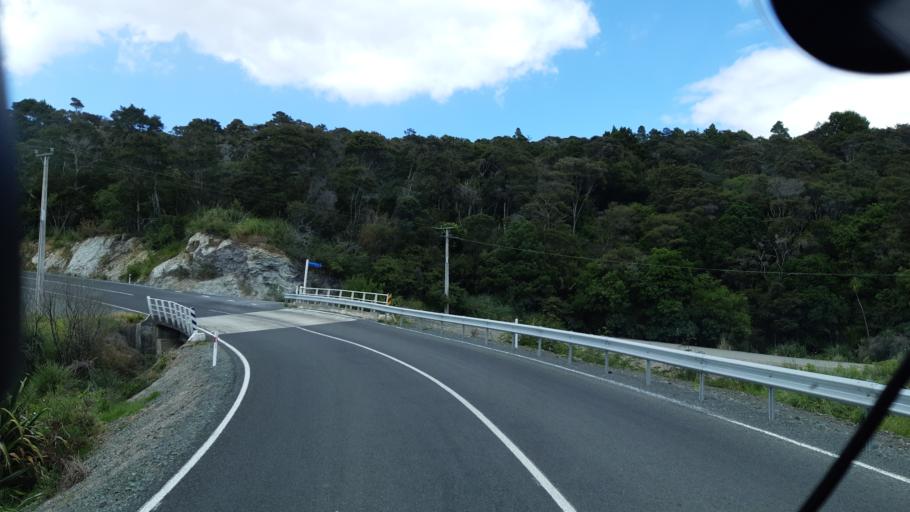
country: NZ
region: Northland
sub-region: Far North District
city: Taipa
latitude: -35.2429
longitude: 173.5344
